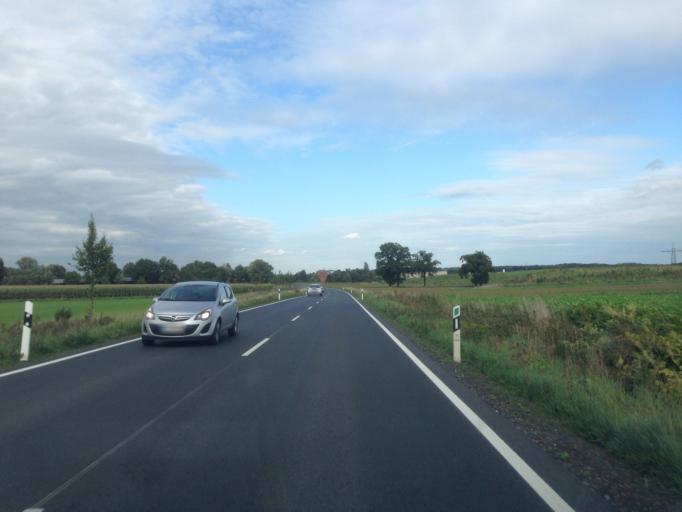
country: DE
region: North Rhine-Westphalia
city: Ludinghausen
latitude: 51.7435
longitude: 7.4210
